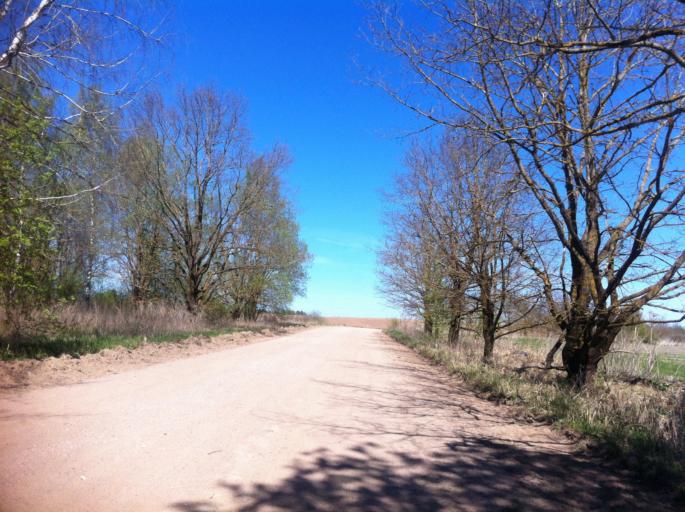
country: RU
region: Pskov
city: Izborsk
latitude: 57.7963
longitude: 27.9640
